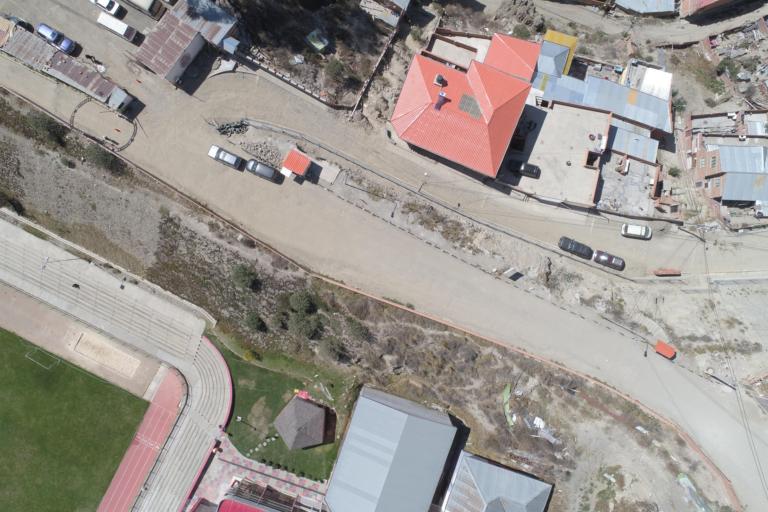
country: BO
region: La Paz
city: La Paz
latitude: -16.5175
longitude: -68.1245
